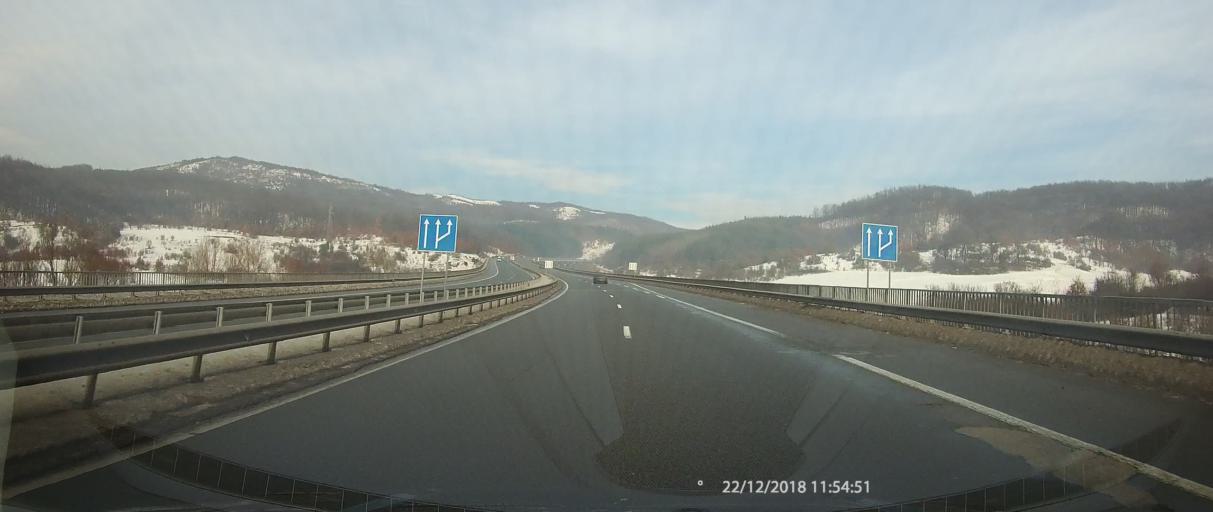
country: BG
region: Pernik
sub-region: Obshtina Pernik
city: Pernik
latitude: 42.6467
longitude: 23.1315
